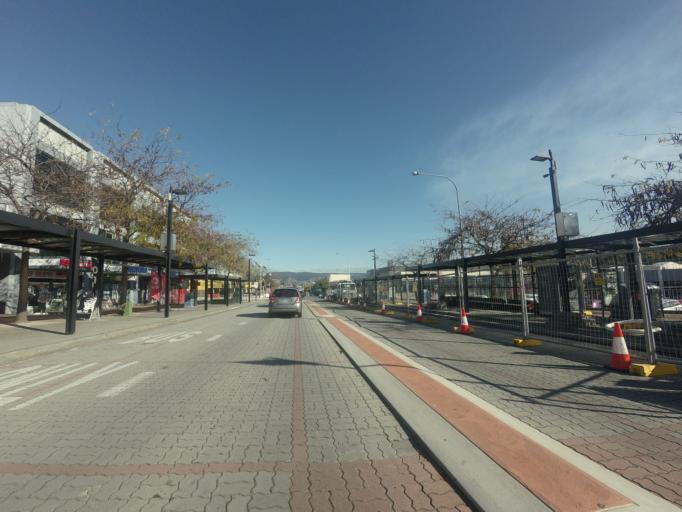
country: AU
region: Tasmania
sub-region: Clarence
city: Bellerive
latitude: -42.8657
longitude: 147.3696
